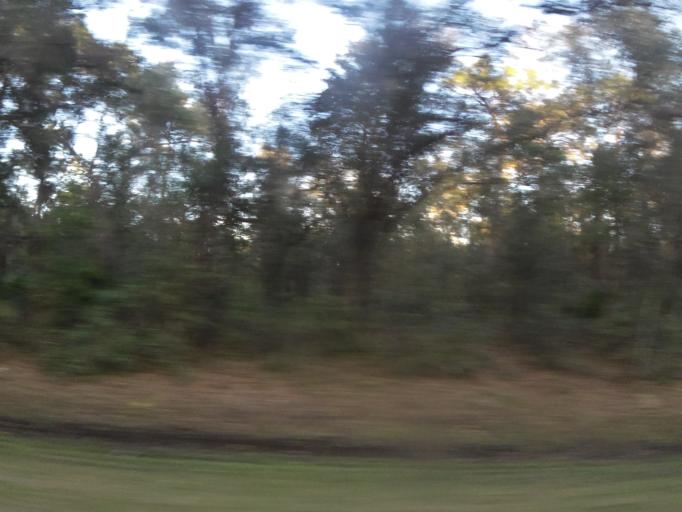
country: US
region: Florida
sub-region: Clay County
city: Green Cove Springs
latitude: 29.8863
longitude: -81.5630
